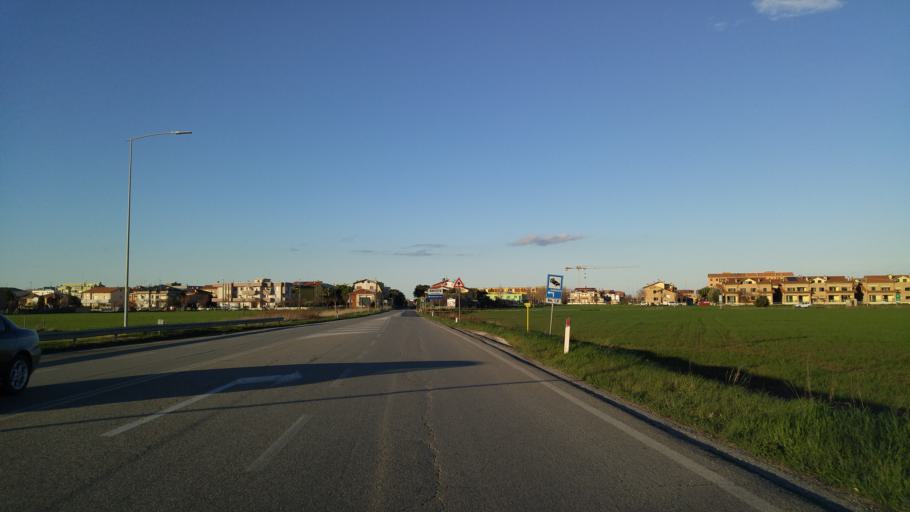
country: IT
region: The Marches
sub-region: Provincia di Pesaro e Urbino
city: Marotta
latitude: 43.7614
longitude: 13.1368
